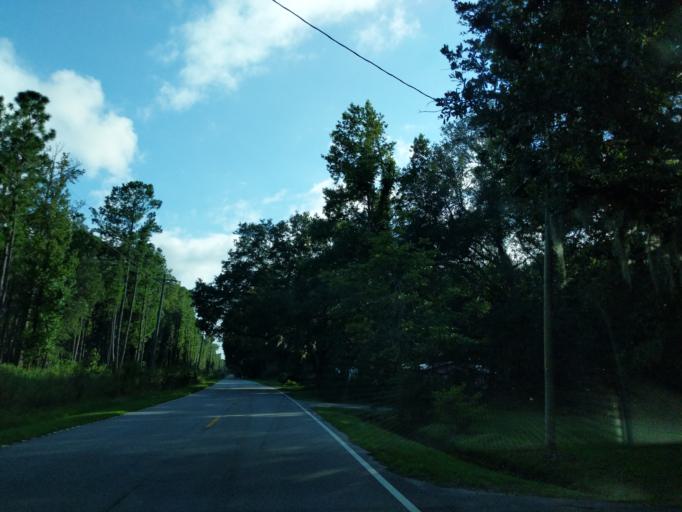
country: US
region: South Carolina
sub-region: Charleston County
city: Awendaw
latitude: 33.1472
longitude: -79.4158
